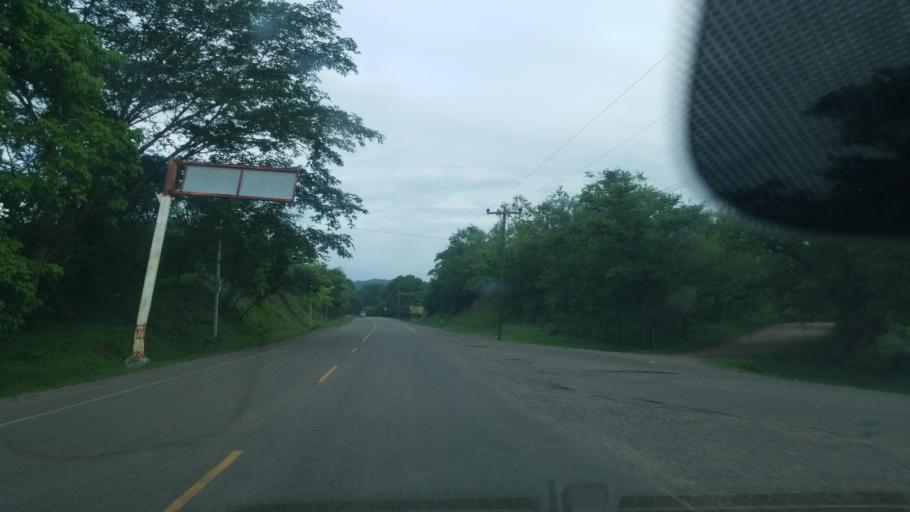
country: HN
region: Santa Barbara
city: San Vicente Centenario
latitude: 14.8800
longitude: -88.2486
